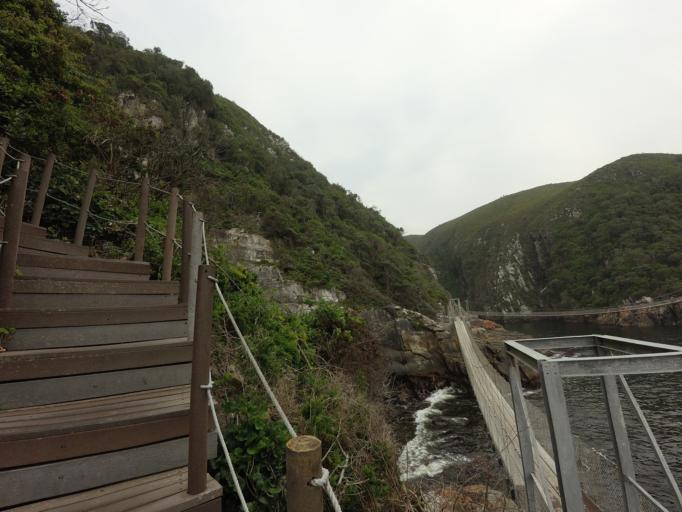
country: ZA
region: Eastern Cape
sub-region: Cacadu District Municipality
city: Kareedouw
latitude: -34.0200
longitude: 23.9024
